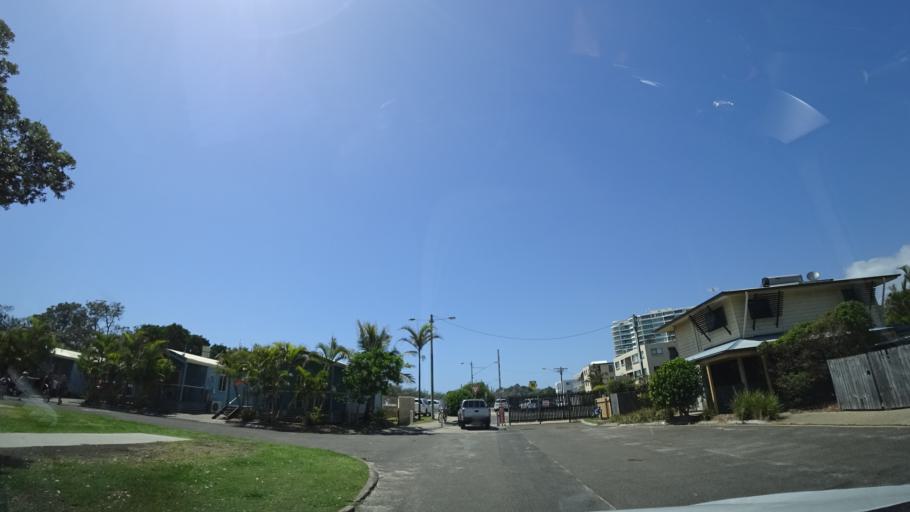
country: AU
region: Queensland
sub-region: Sunshine Coast
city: Mooloolaba
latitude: -26.6530
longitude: 153.1019
